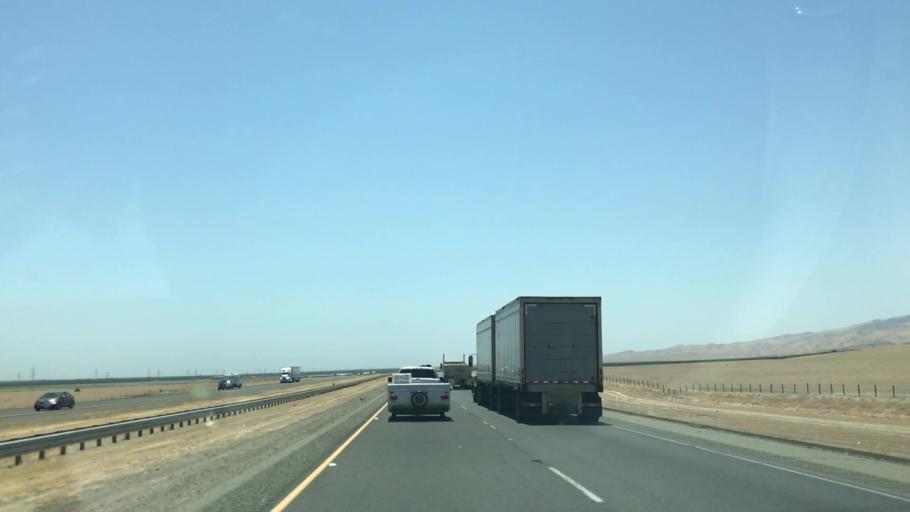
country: US
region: California
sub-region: Fresno County
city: San Joaquin
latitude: 36.4675
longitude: -120.4253
